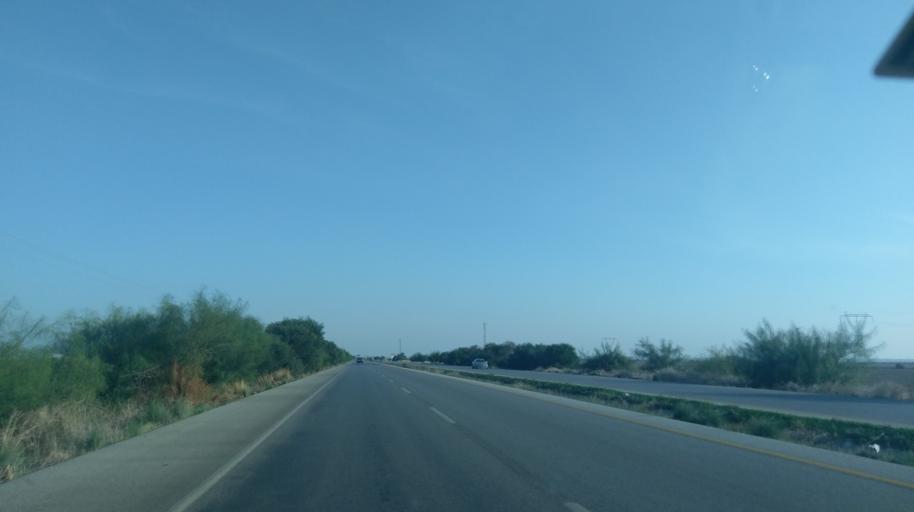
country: CY
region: Ammochostos
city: Acheritou
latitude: 35.1630
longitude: 33.8301
